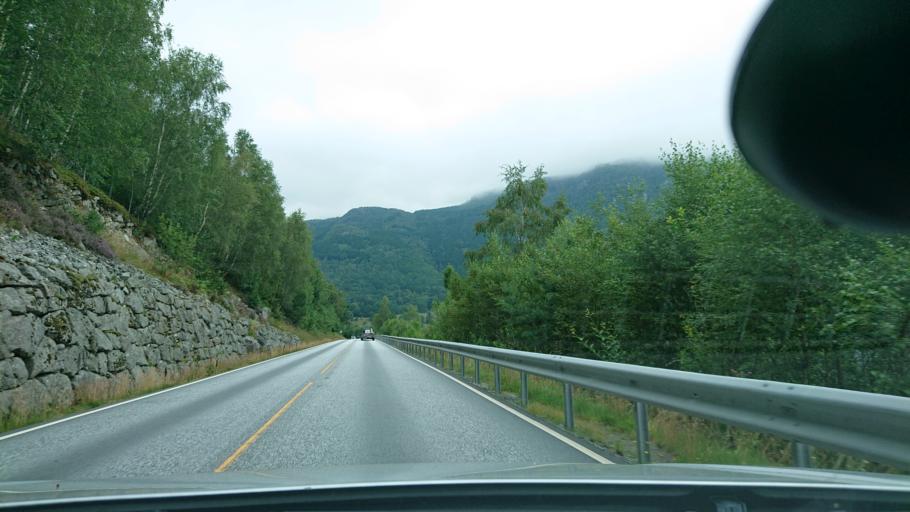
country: NO
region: Rogaland
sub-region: Hjelmeland
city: Hjelmelandsvagen
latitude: 59.1569
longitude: 6.1741
